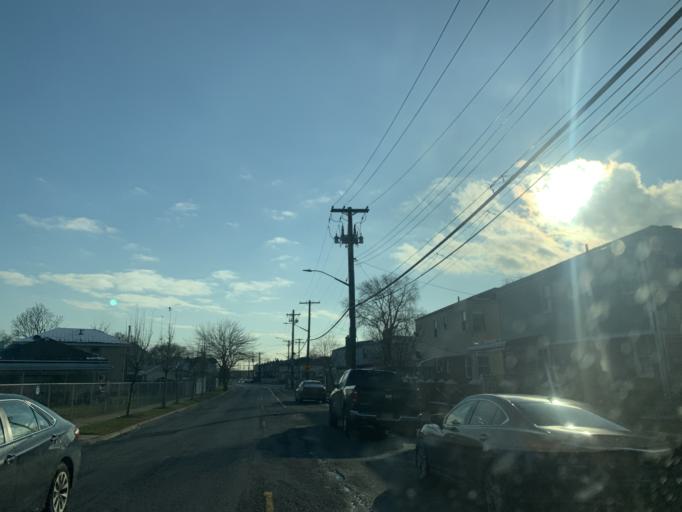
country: US
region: New York
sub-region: Queens County
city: Jamaica
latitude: 40.6816
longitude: -73.8079
